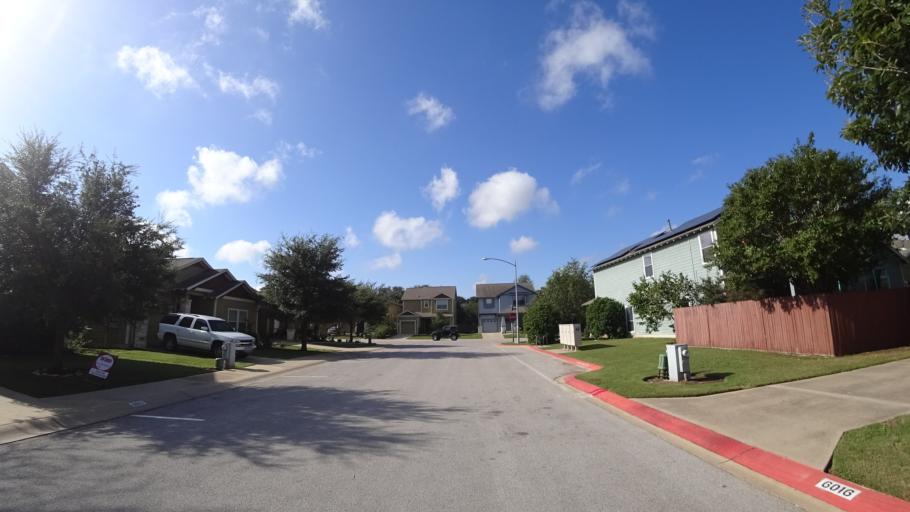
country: US
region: Texas
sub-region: Travis County
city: Rollingwood
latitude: 30.2141
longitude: -97.8060
